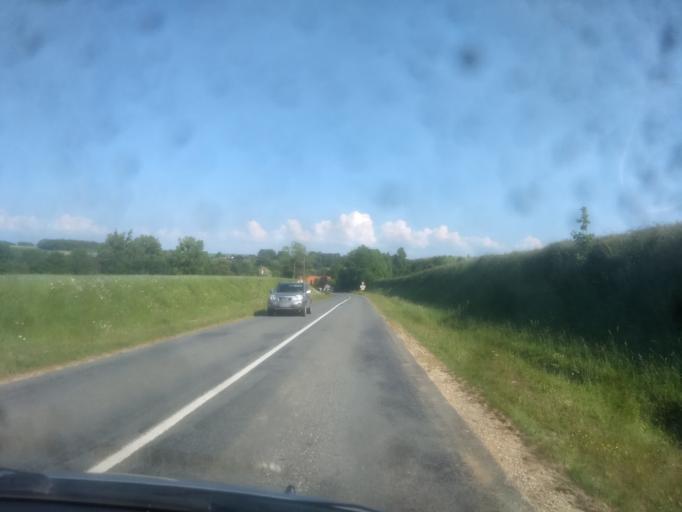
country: FR
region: Picardie
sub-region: Departement de la Somme
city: Crecy-en-Ponthieu
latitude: 50.1721
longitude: 1.8695
